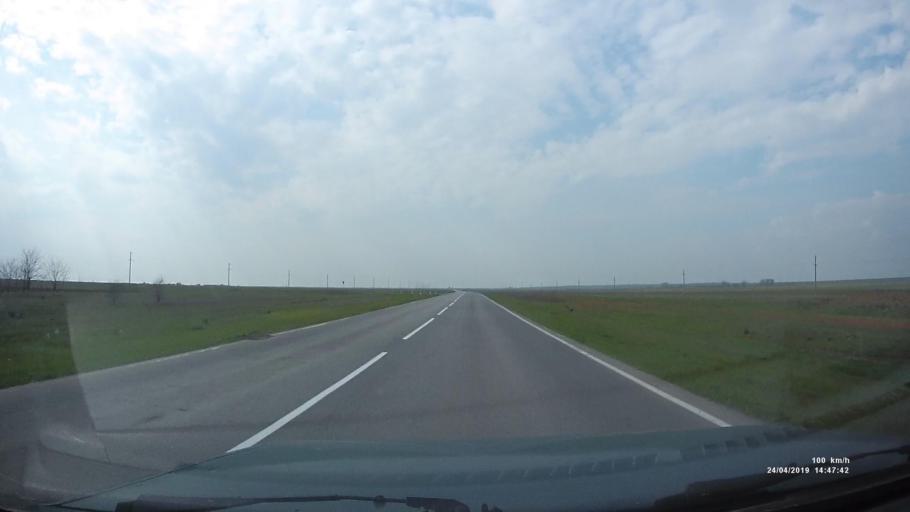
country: RU
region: Rostov
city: Remontnoye
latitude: 46.4939
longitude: 43.7686
